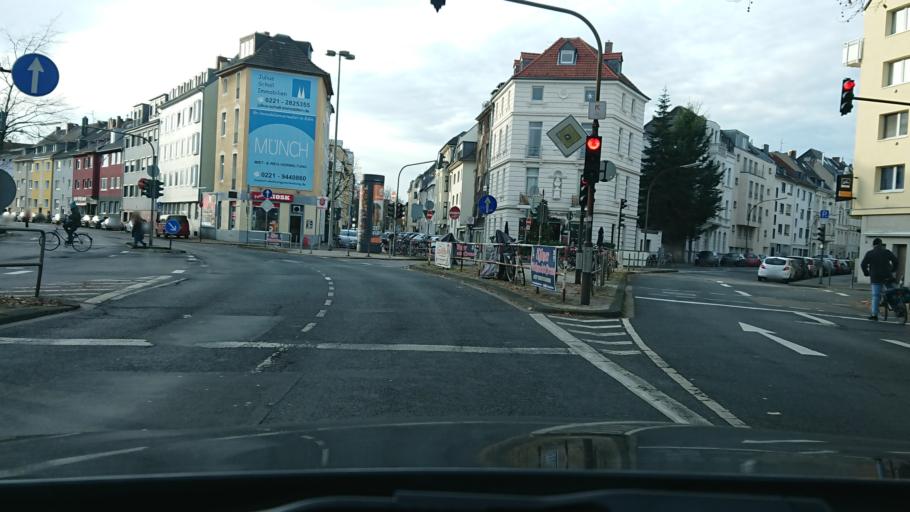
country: DE
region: North Rhine-Westphalia
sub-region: Regierungsbezirk Koln
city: Neustadt/Sued
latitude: 50.9305
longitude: 6.9219
